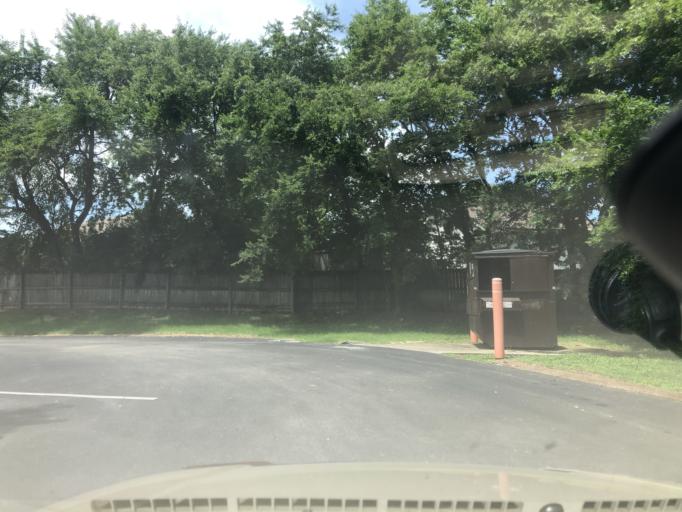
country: US
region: Tennessee
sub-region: Davidson County
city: Goodlettsville
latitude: 36.2587
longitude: -86.7053
